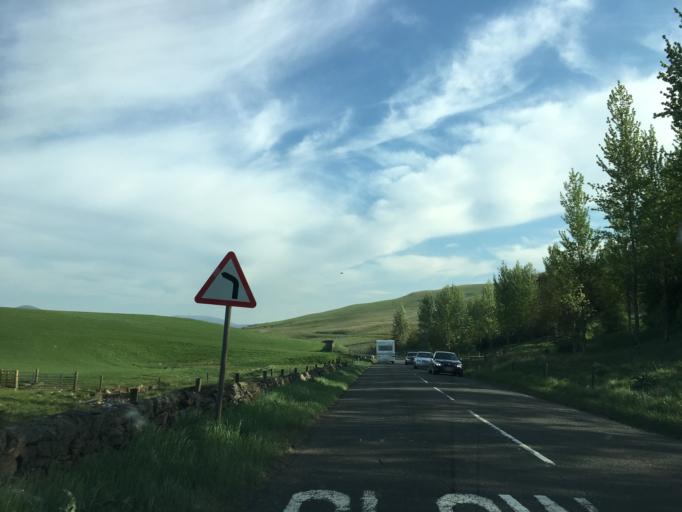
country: GB
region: Scotland
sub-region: South Lanarkshire
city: Biggar
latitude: 55.6383
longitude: -3.4257
